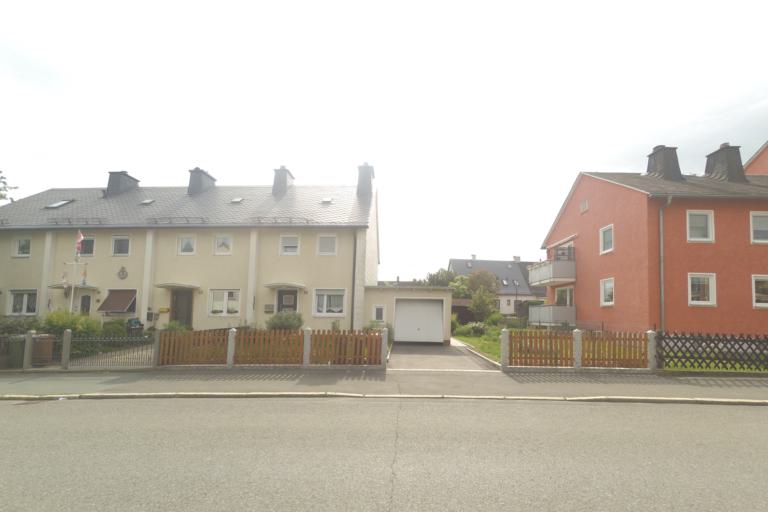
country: DE
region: Bavaria
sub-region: Upper Franconia
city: Munchberg
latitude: 50.1842
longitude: 11.7912
